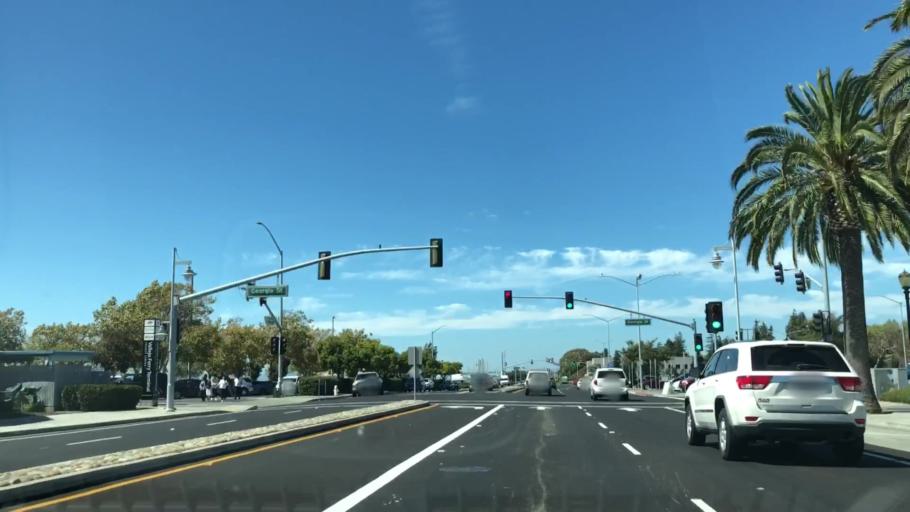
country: US
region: California
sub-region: Solano County
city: Vallejo
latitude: 38.1006
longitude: -122.2625
